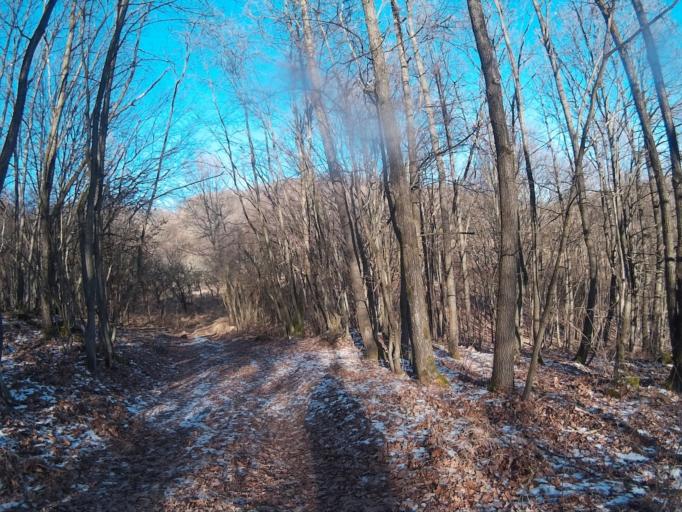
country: HU
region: Borsod-Abauj-Zemplen
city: Rudabanya
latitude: 48.4907
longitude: 20.5828
